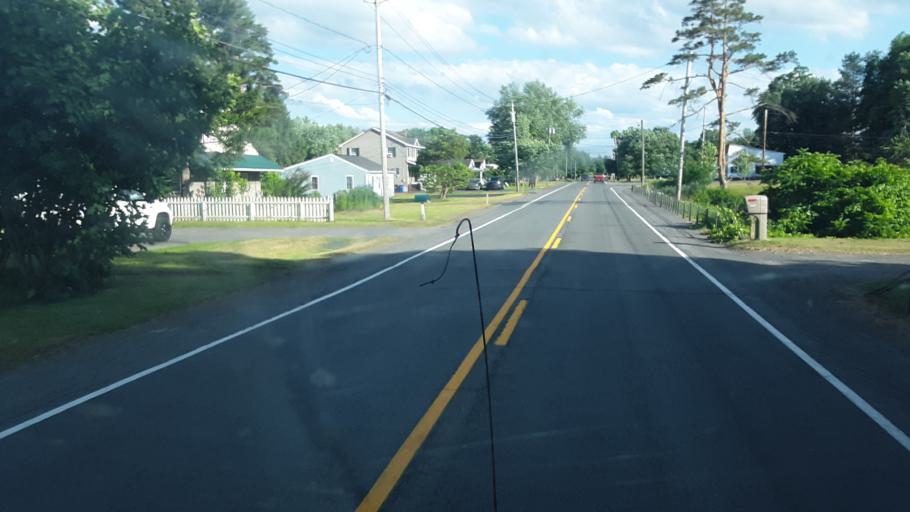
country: US
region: New York
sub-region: Oneida County
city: Rome
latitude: 43.2701
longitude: -75.4670
